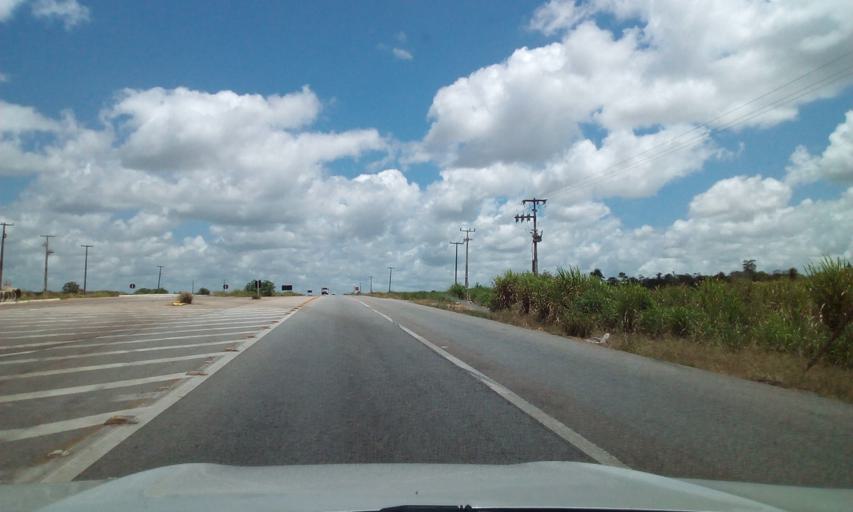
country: BR
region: Alagoas
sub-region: Campo Alegre
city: Campo Alegre
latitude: -9.9054
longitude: -36.3156
